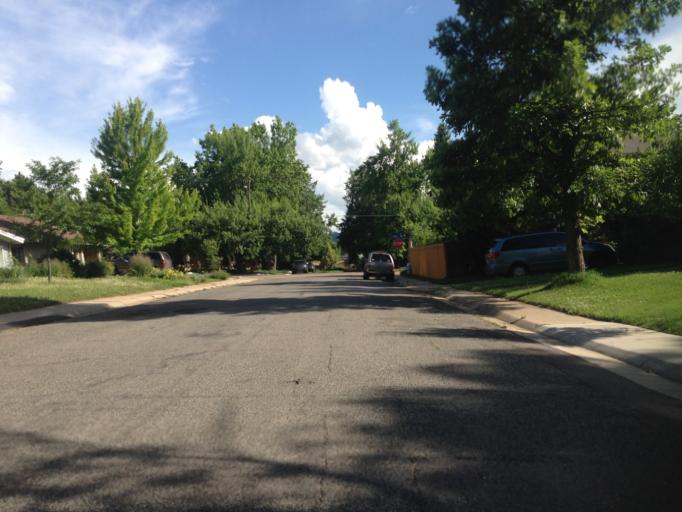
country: US
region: Colorado
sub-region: Boulder County
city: Boulder
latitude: 40.0306
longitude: -105.2752
